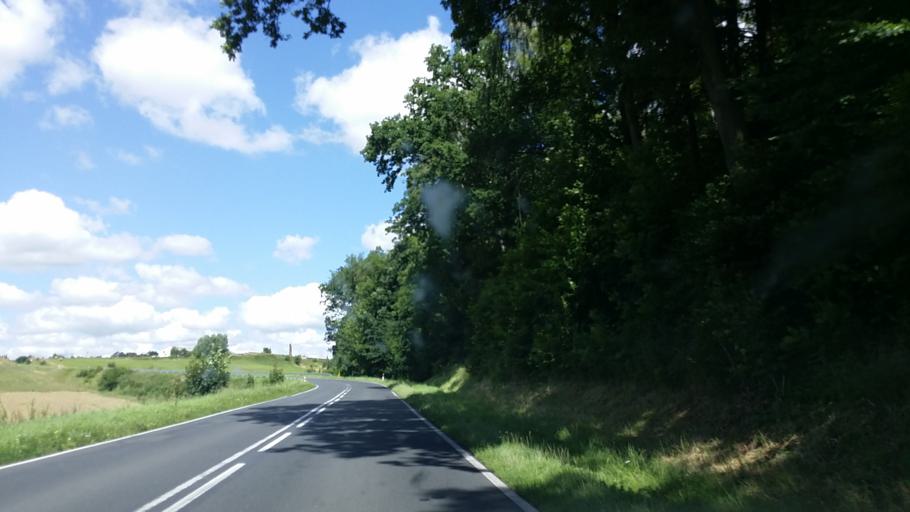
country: PL
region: West Pomeranian Voivodeship
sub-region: Powiat swidwinski
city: Swidwin
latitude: 53.8057
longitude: 15.7699
